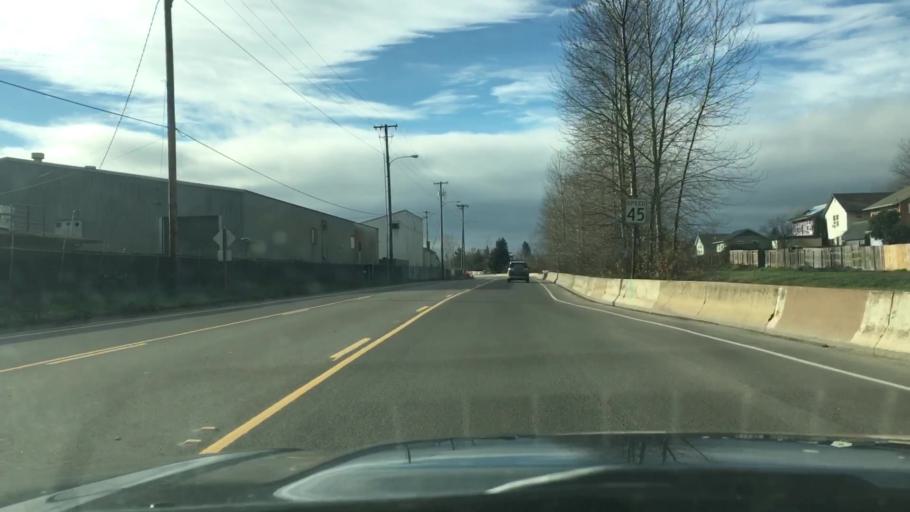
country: US
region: Oregon
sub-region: Lane County
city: Eugene
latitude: 44.0639
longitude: -123.1442
